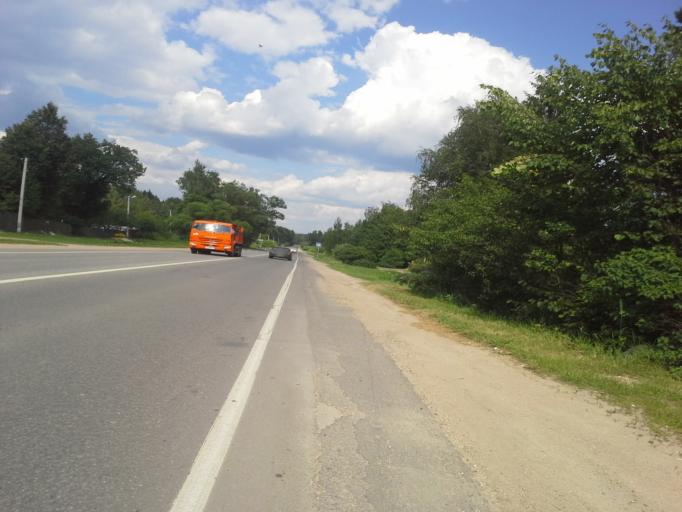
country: RU
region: Moskovskaya
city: Naro-Fominsk
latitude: 55.3974
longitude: 36.7738
